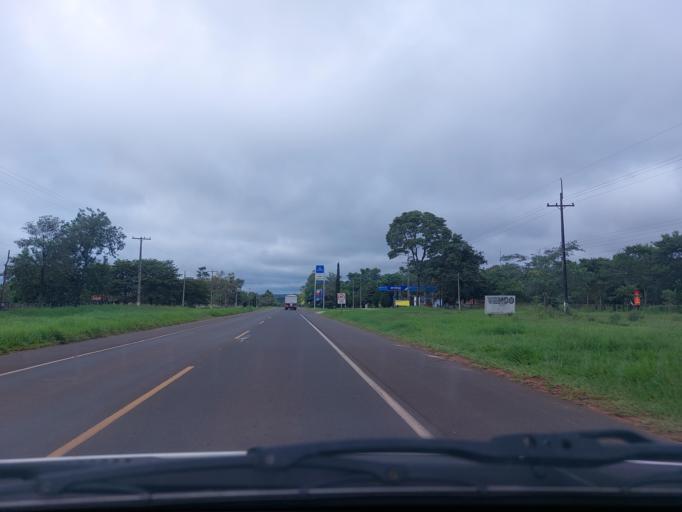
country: PY
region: San Pedro
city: Guayaybi
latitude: -24.6188
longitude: -56.3807
